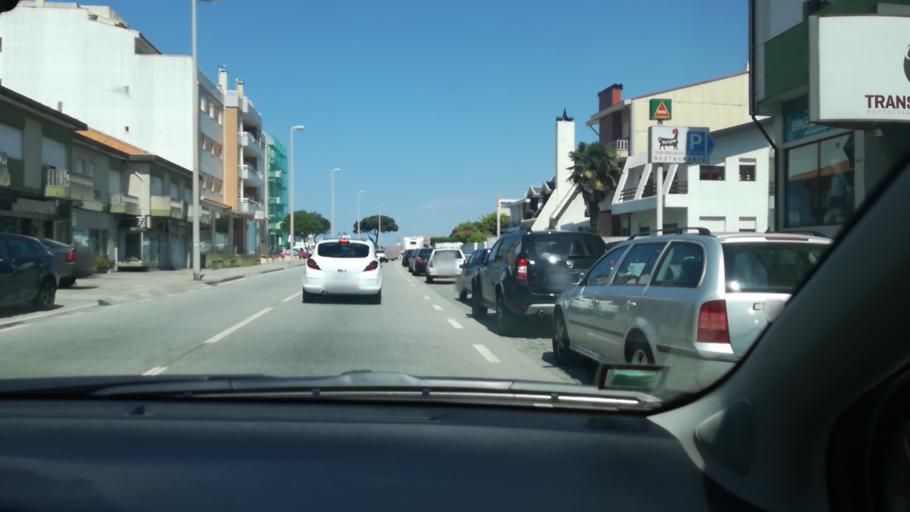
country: PT
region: Porto
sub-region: Povoa de Varzim
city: Povoa de Varzim
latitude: 41.3895
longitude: -8.7662
